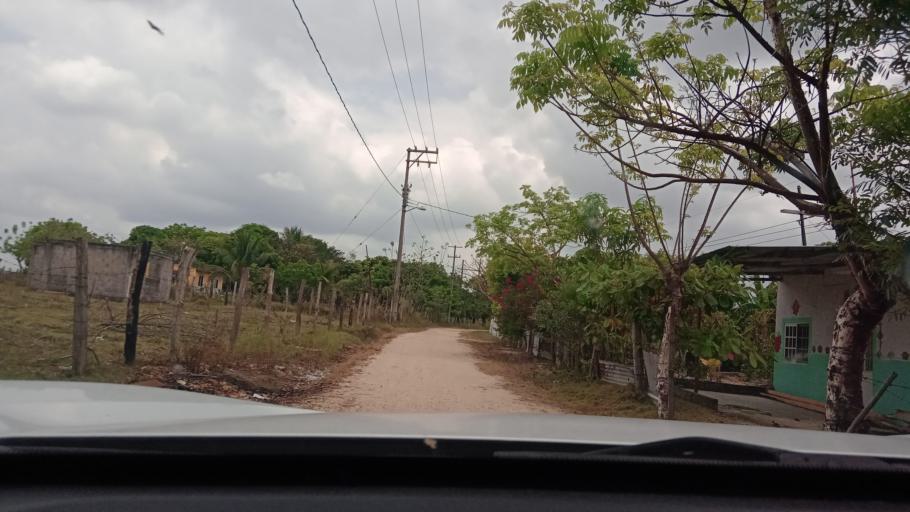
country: MX
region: Veracruz
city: Las Choapas
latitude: 17.8913
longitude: -94.1149
